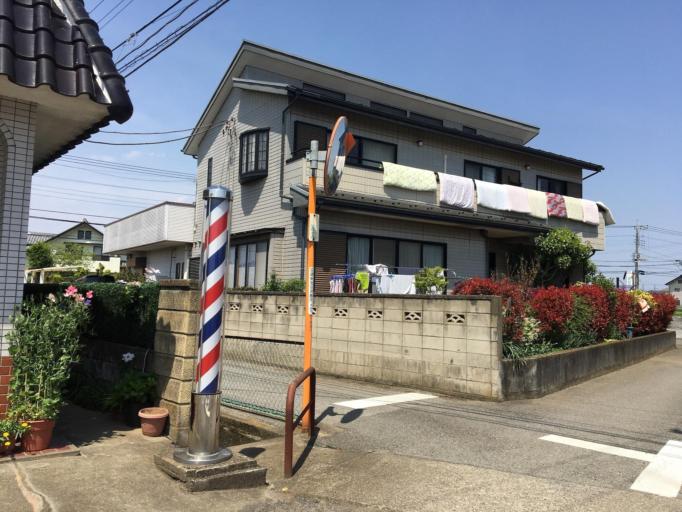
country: JP
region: Gunma
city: Ota
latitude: 36.2829
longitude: 139.3254
